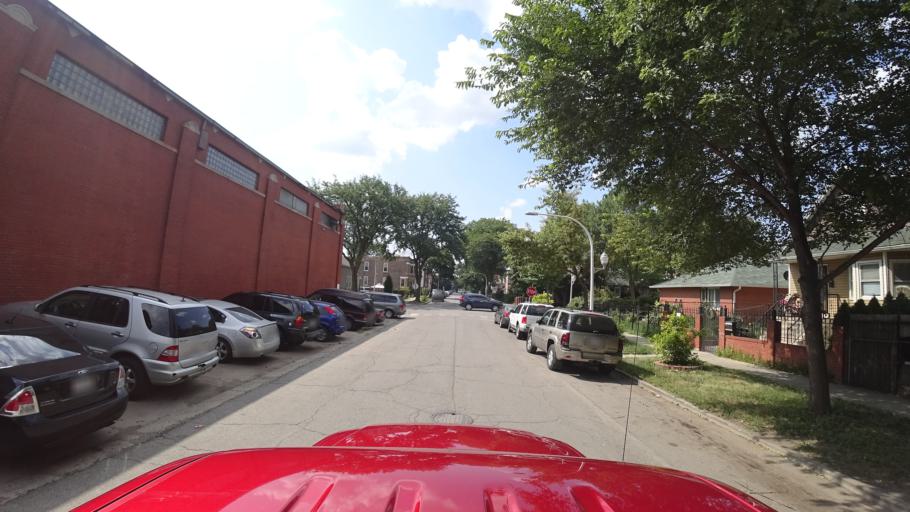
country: US
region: Illinois
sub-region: Cook County
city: Chicago
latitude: 41.8250
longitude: -87.6996
